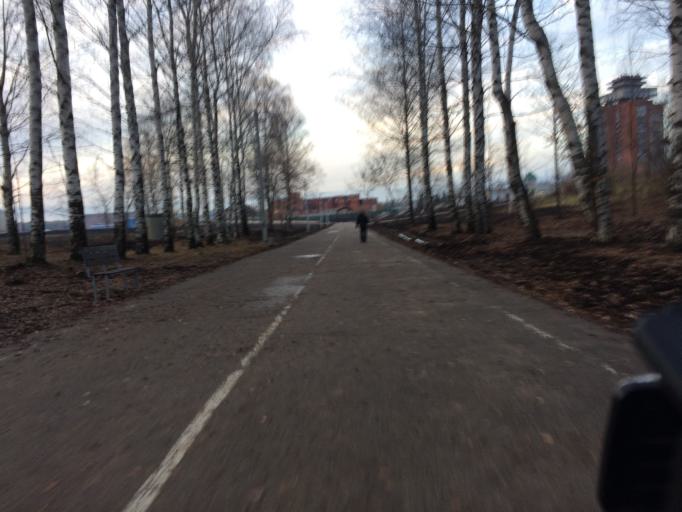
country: RU
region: Mariy-El
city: Yoshkar-Ola
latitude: 56.6250
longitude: 47.9095
